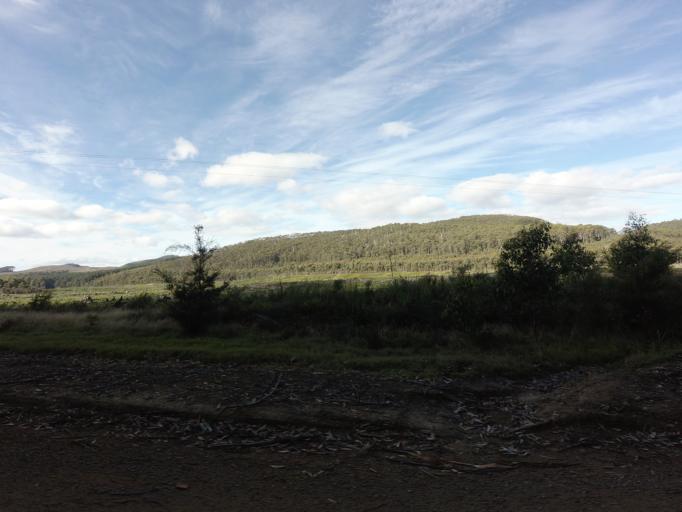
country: AU
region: Tasmania
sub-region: Clarence
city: Sandford
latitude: -43.1681
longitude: 147.7678
